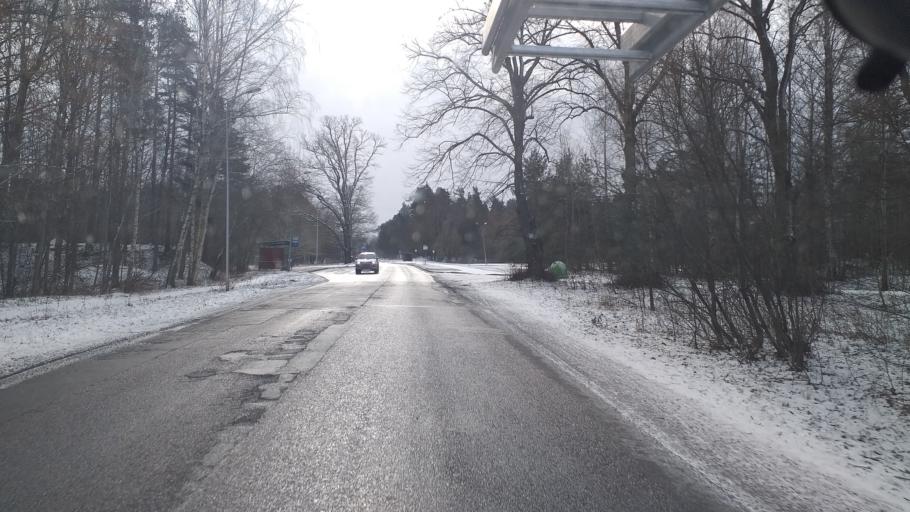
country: LV
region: Riga
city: Bolderaja
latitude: 56.9848
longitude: 24.0325
